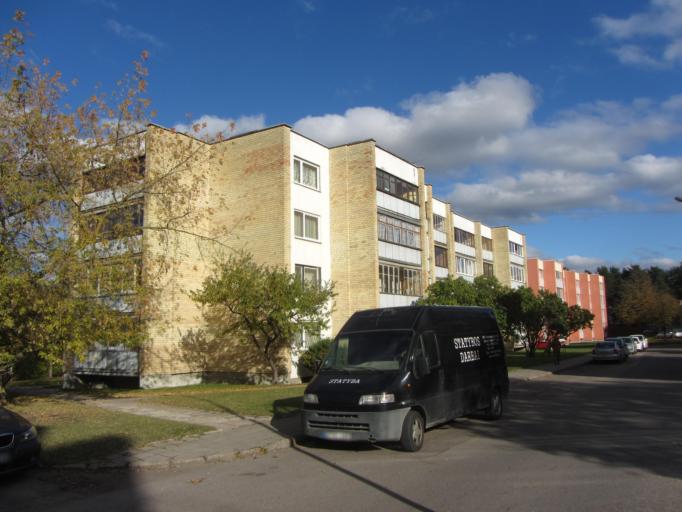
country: LT
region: Vilnius County
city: Lazdynai
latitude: 54.6705
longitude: 25.2157
